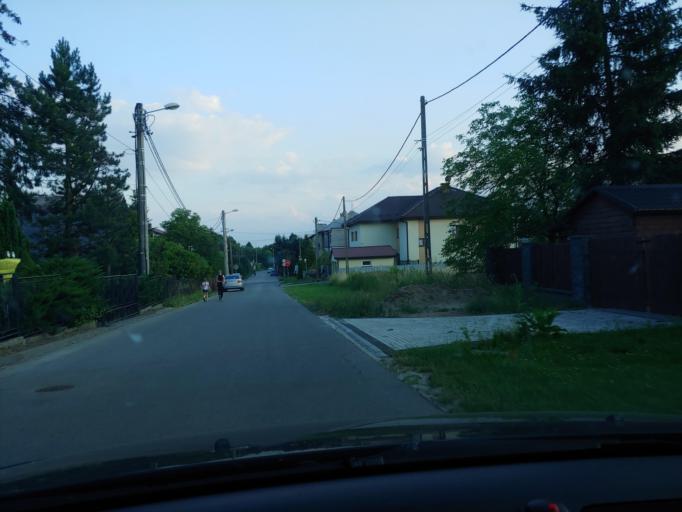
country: PL
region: Lesser Poland Voivodeship
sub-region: Powiat chrzanowski
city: Trzebinia
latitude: 50.1683
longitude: 19.4700
